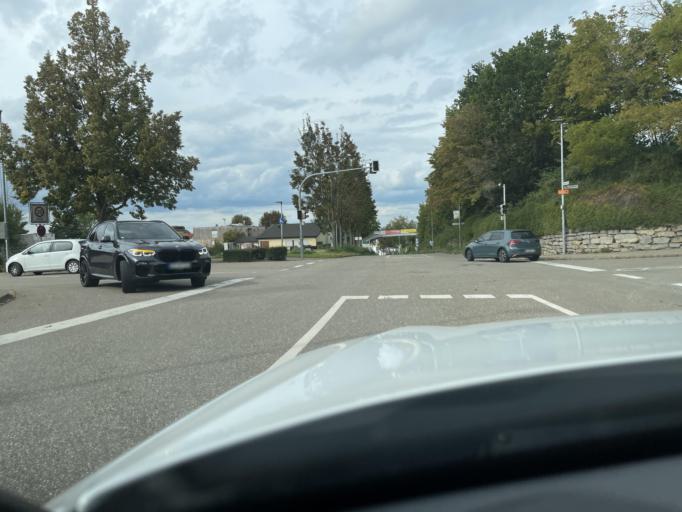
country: DE
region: Baden-Wuerttemberg
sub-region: Regierungsbezirk Stuttgart
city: Marbach am Neckar
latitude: 48.9341
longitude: 9.2620
